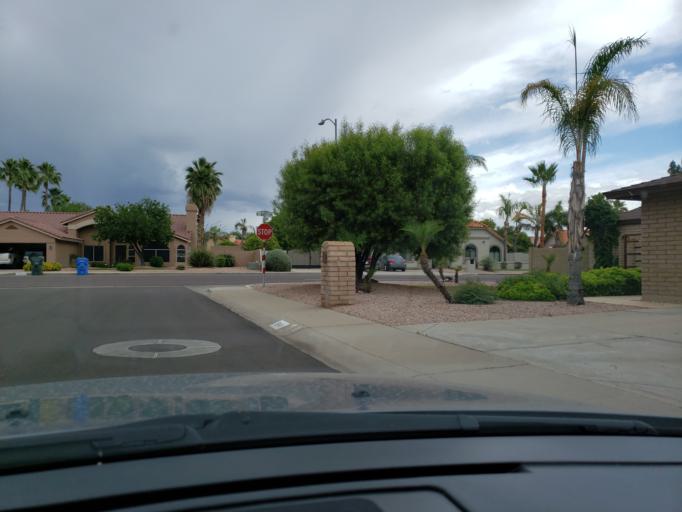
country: US
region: Arizona
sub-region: Maricopa County
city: Paradise Valley
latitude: 33.6174
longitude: -111.9522
